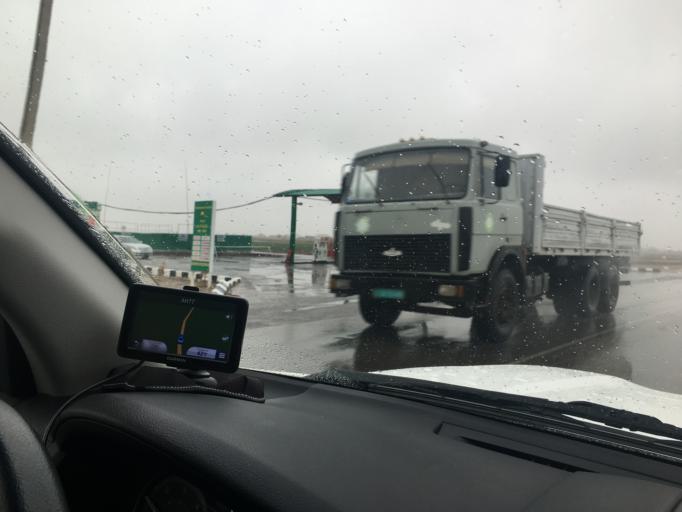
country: TM
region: Mary
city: Bayramaly
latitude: 37.4092
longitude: 62.1691
